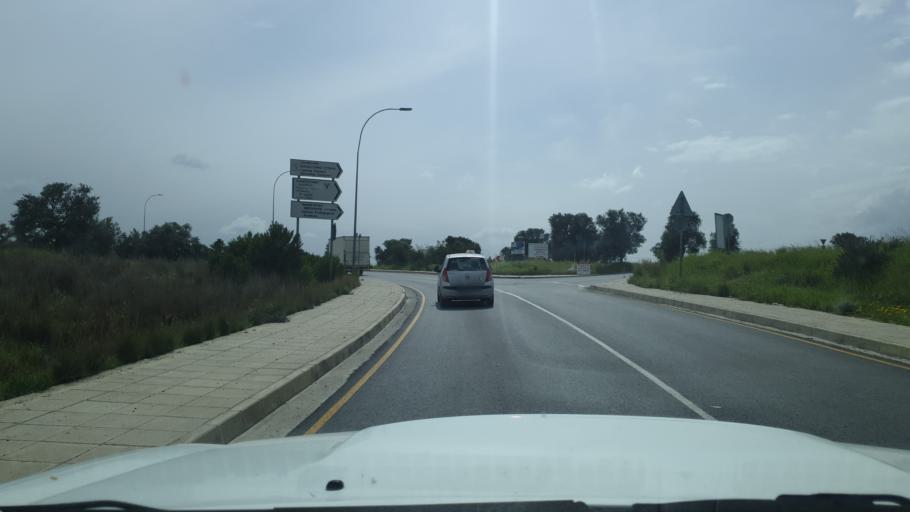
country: CY
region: Lefkosia
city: Geri
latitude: 35.1042
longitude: 33.3670
